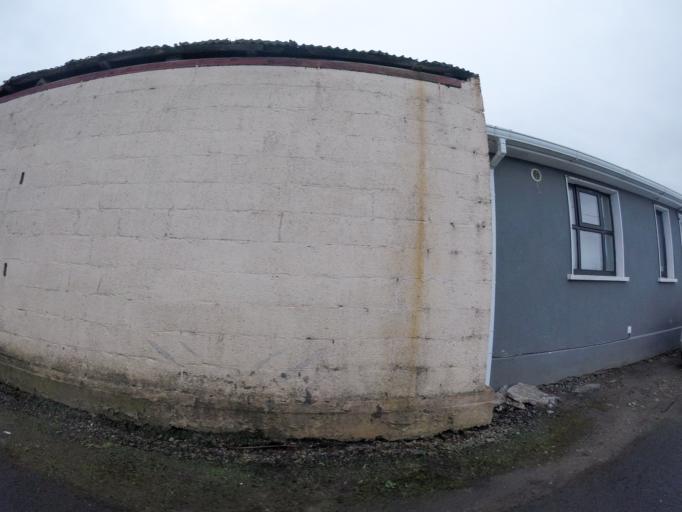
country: IE
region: Munster
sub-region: Waterford
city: Waterford
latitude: 52.2717
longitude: -6.9958
